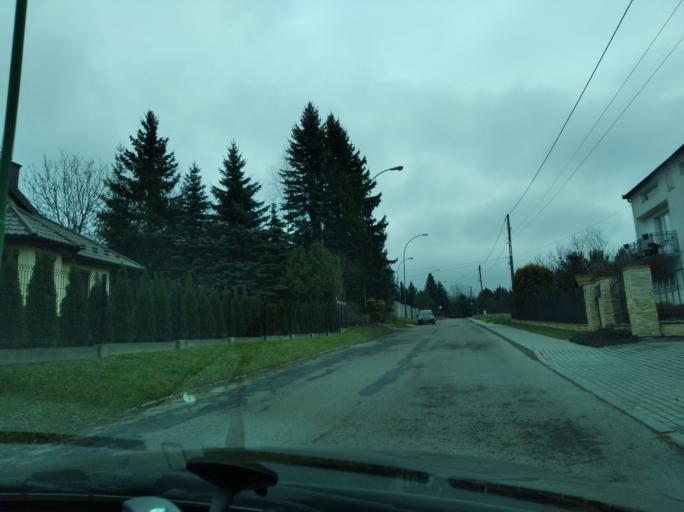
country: PL
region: Subcarpathian Voivodeship
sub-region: Powiat lancucki
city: Lancut
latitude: 50.0634
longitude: 22.2147
